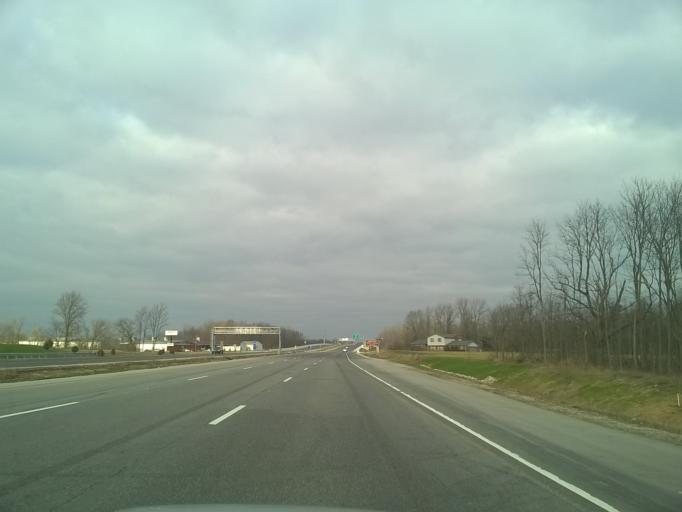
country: US
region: Indiana
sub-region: Hamilton County
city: Westfield
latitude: 40.0278
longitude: -86.1336
